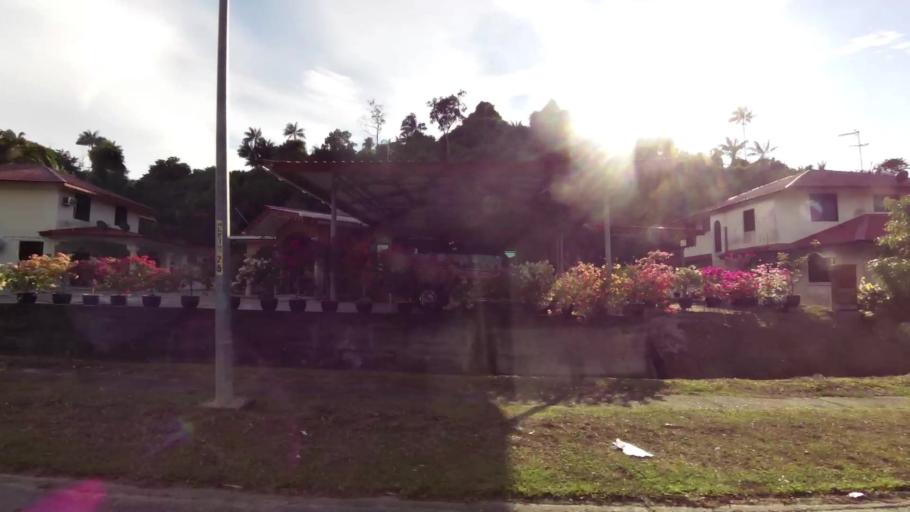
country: BN
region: Brunei and Muara
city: Bandar Seri Begawan
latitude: 4.9842
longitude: 114.9669
